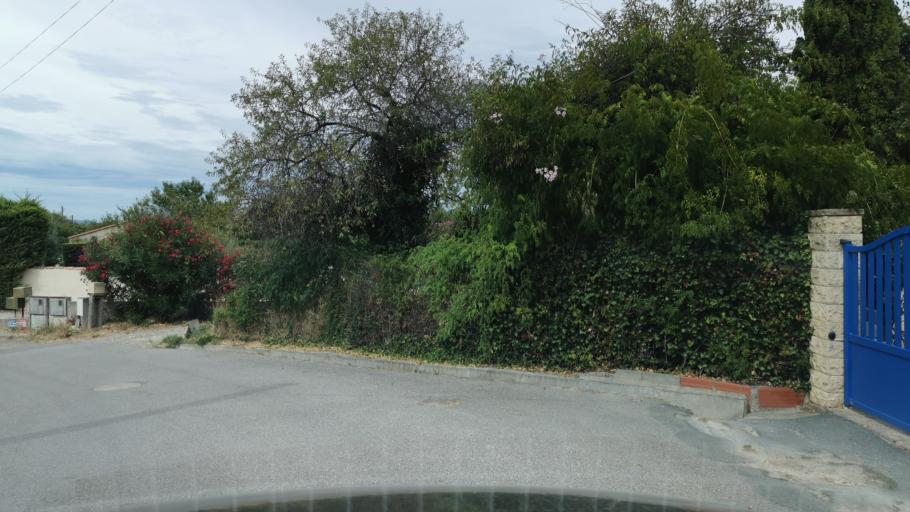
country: FR
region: Languedoc-Roussillon
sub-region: Departement de l'Aude
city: Marcorignan
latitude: 43.2274
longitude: 2.9278
